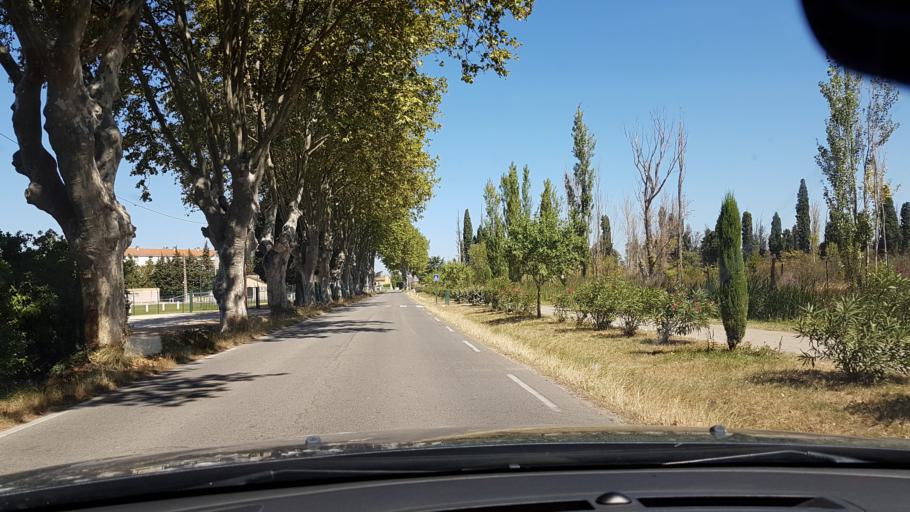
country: FR
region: Provence-Alpes-Cote d'Azur
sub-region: Departement des Bouches-du-Rhone
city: Saint-Andiol
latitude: 43.8282
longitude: 4.9449
